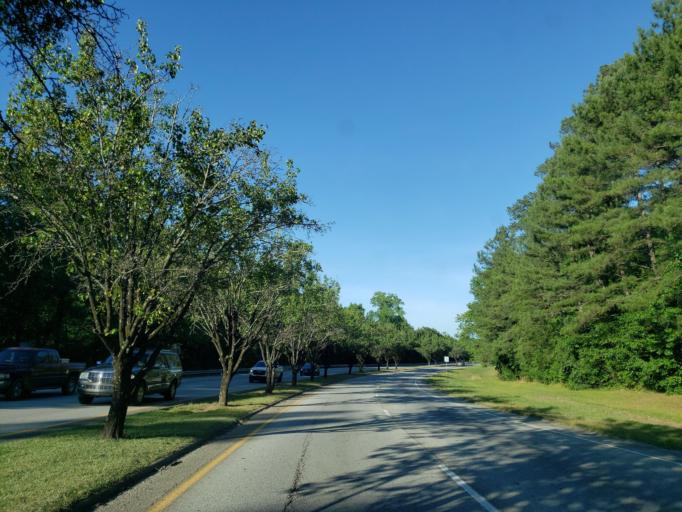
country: US
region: Georgia
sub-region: Floyd County
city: Rome
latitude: 34.2809
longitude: -85.1796
